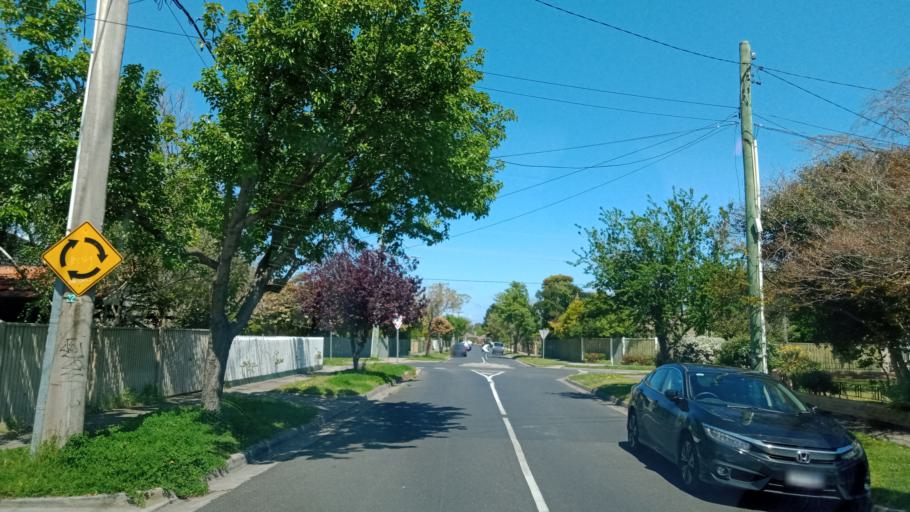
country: AU
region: Victoria
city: Murrumbeena
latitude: -37.9068
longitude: 145.0581
